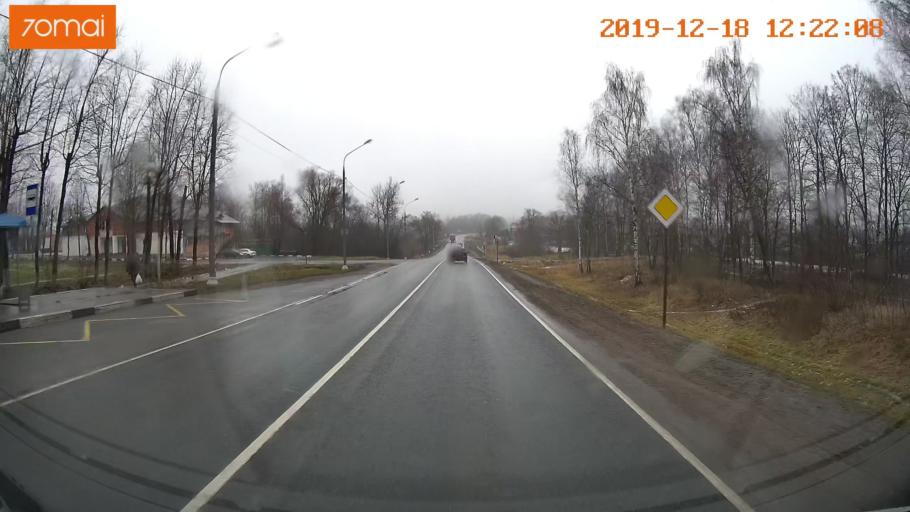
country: RU
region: Moskovskaya
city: Novopetrovskoye
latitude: 56.0033
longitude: 36.4784
